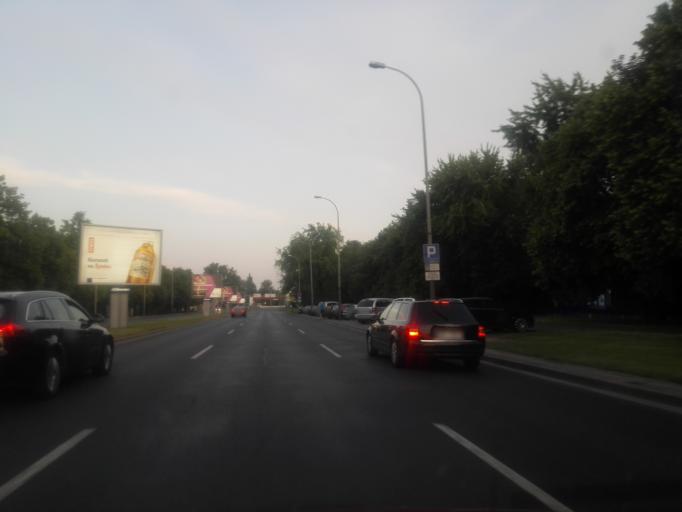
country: PL
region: Masovian Voivodeship
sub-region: Warszawa
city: Wlochy
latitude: 52.1775
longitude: 20.9787
